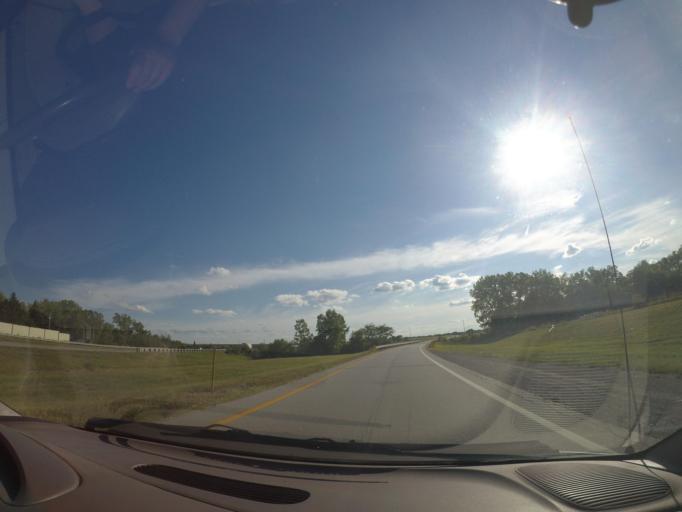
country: US
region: Ohio
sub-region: Henry County
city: Napoleon
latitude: 41.3994
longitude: -84.1449
